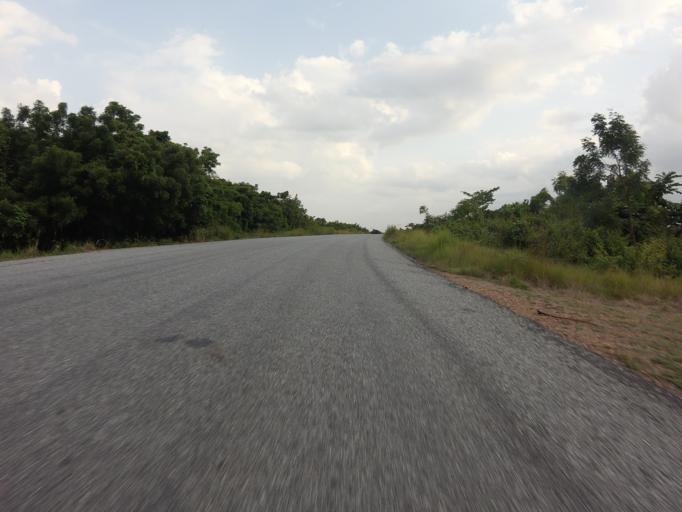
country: GH
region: Volta
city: Ho
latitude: 6.3724
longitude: 0.5335
